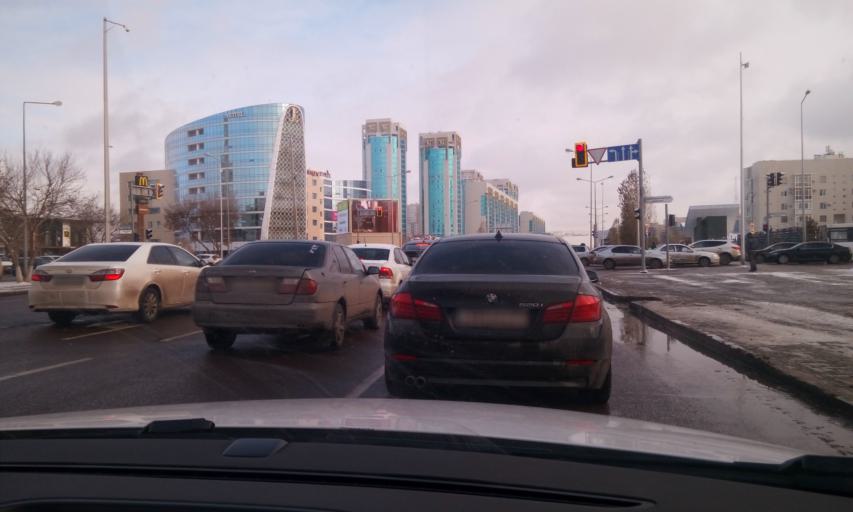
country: KZ
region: Astana Qalasy
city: Astana
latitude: 51.1365
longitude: 71.4150
